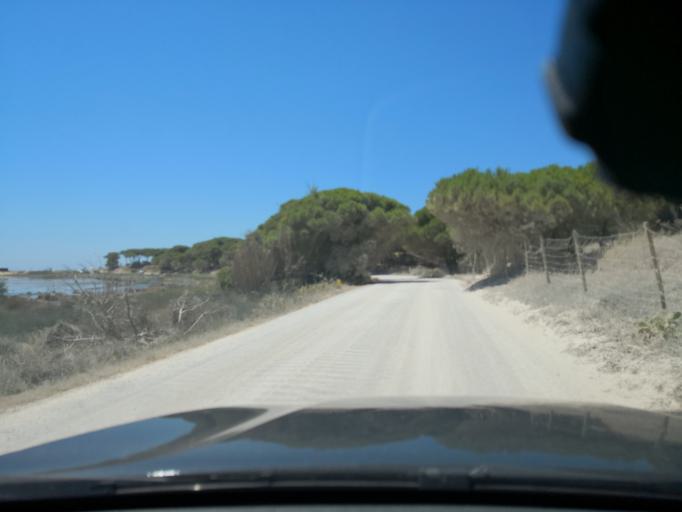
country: PT
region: Faro
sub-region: Loule
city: Quarteira
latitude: 37.0626
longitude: -8.0836
